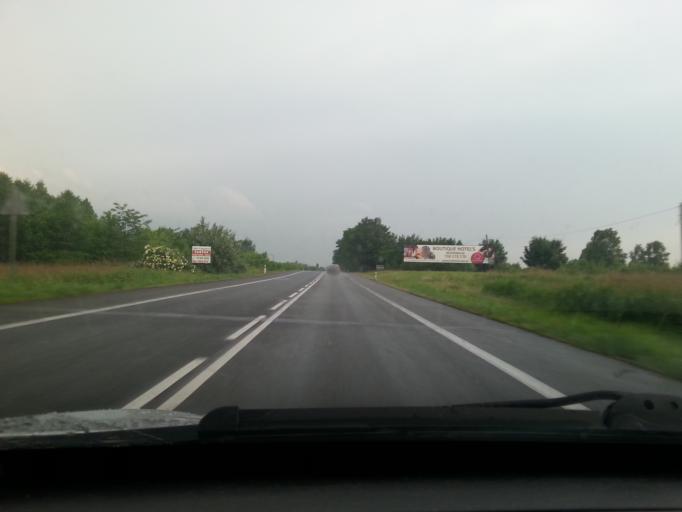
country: PL
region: Lodz Voivodeship
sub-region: Powiat zgierski
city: Strykow
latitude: 51.8628
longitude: 19.5671
